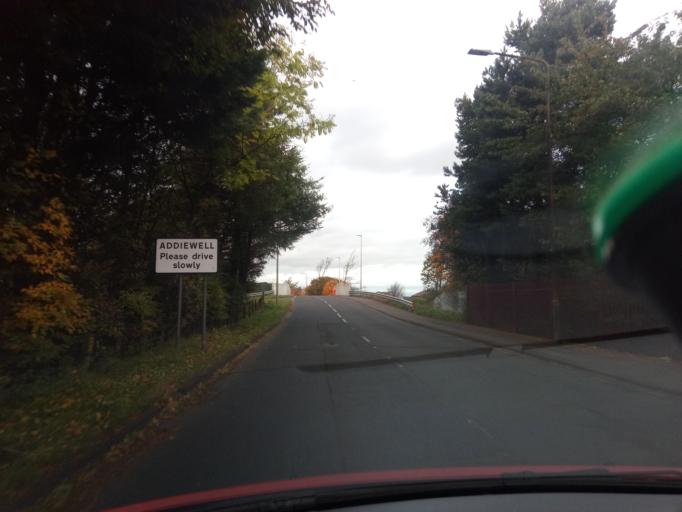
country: GB
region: Scotland
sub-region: West Lothian
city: Blackburn
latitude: 55.8406
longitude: -3.6139
